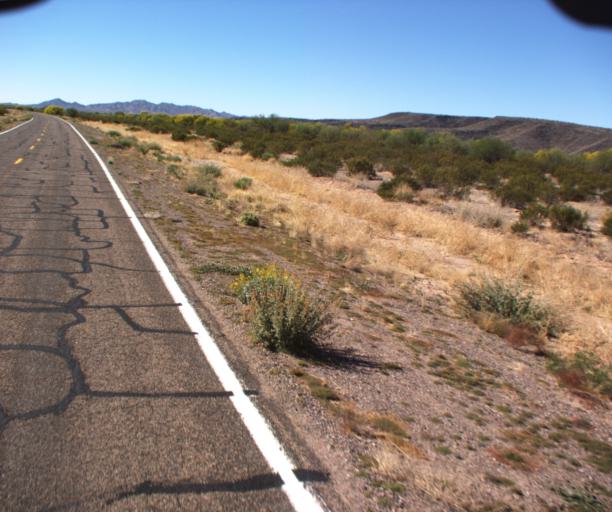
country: US
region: Arizona
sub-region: Pima County
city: Ajo
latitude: 32.4946
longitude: -112.8818
